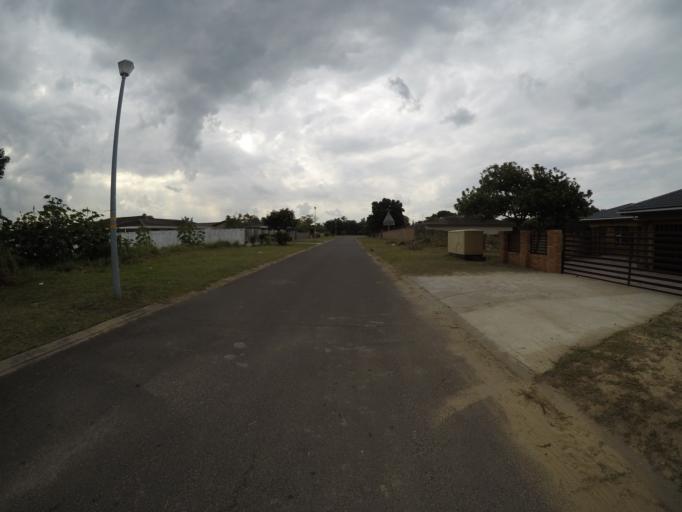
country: ZA
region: KwaZulu-Natal
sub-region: uThungulu District Municipality
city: Richards Bay
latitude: -28.7341
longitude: 32.0444
